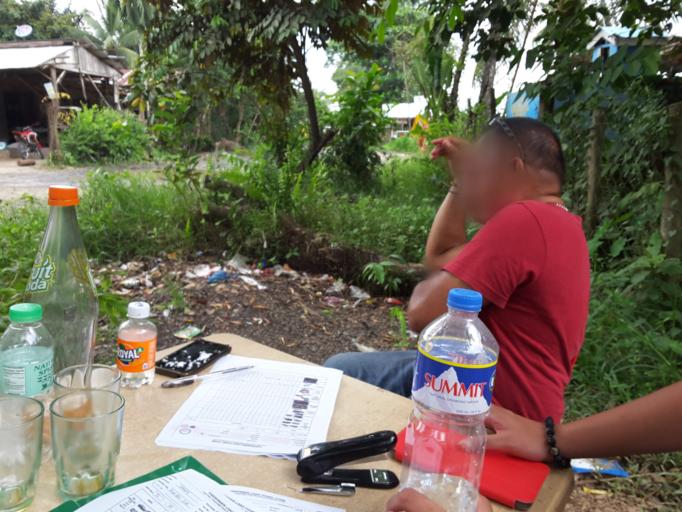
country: PH
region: Caraga
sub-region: Province of Agusan del Sur
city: La Paz
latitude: 8.2725
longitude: 125.8091
